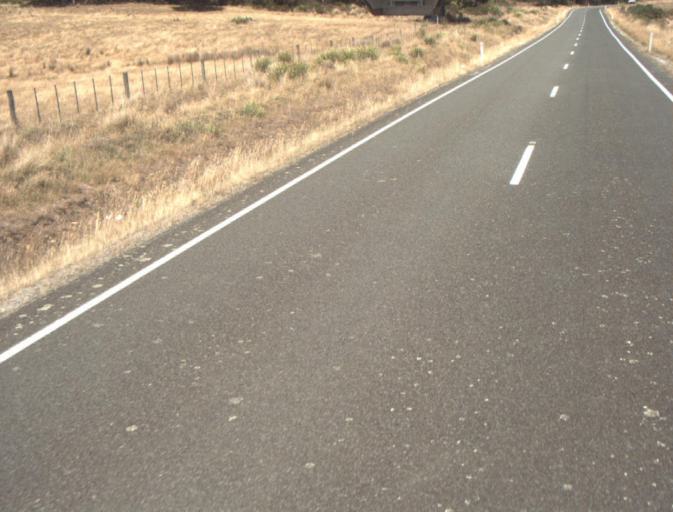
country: AU
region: Tasmania
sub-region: Dorset
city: Scottsdale
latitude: -41.2942
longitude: 147.3853
